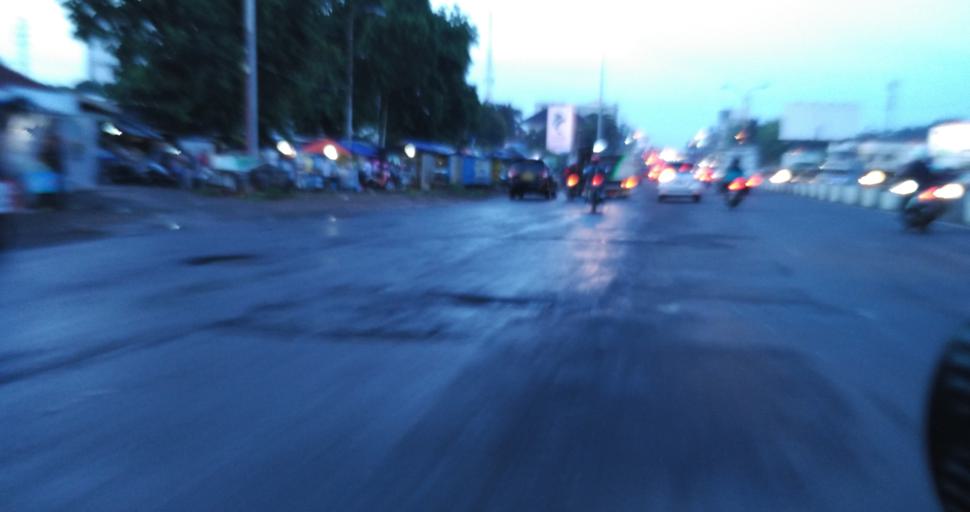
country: ID
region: Central Java
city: Semarang
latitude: -7.0325
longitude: 110.4179
